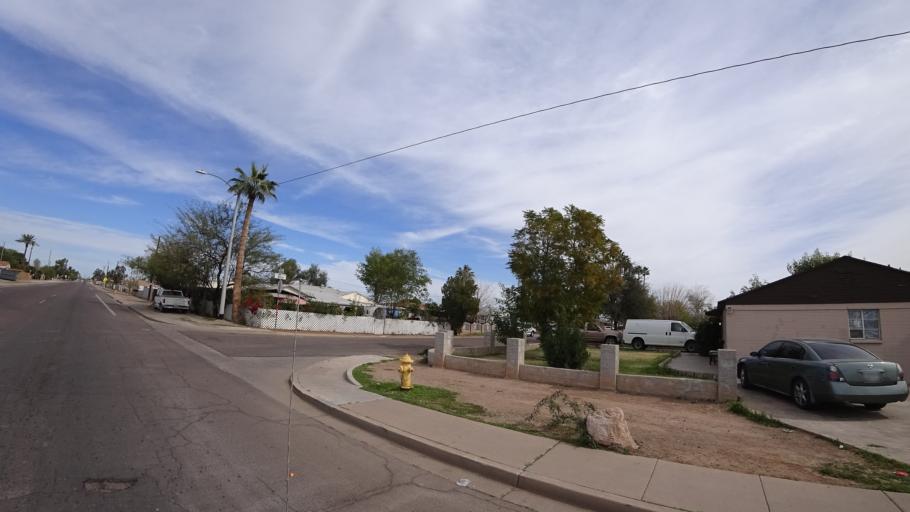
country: US
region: Arizona
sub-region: Maricopa County
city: Phoenix
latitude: 33.4563
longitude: -112.1259
